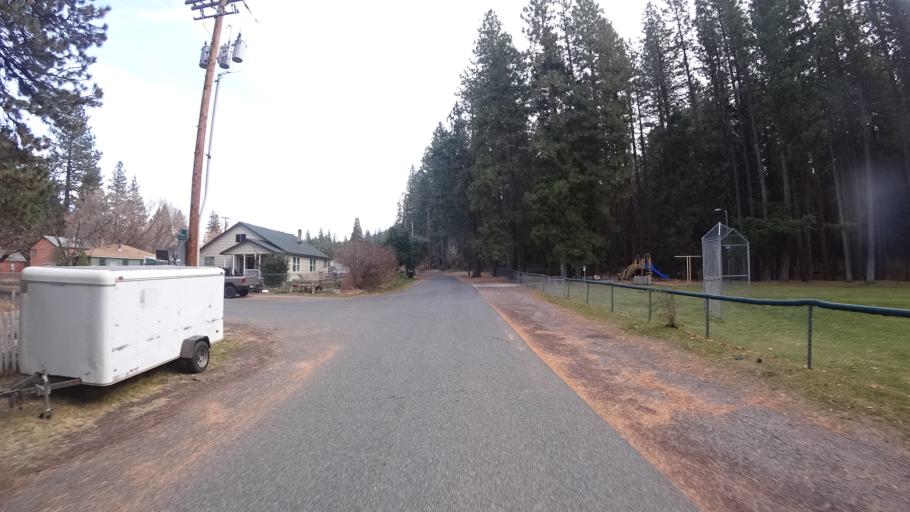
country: US
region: California
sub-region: Siskiyou County
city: Weed
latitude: 41.4450
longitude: -122.3639
